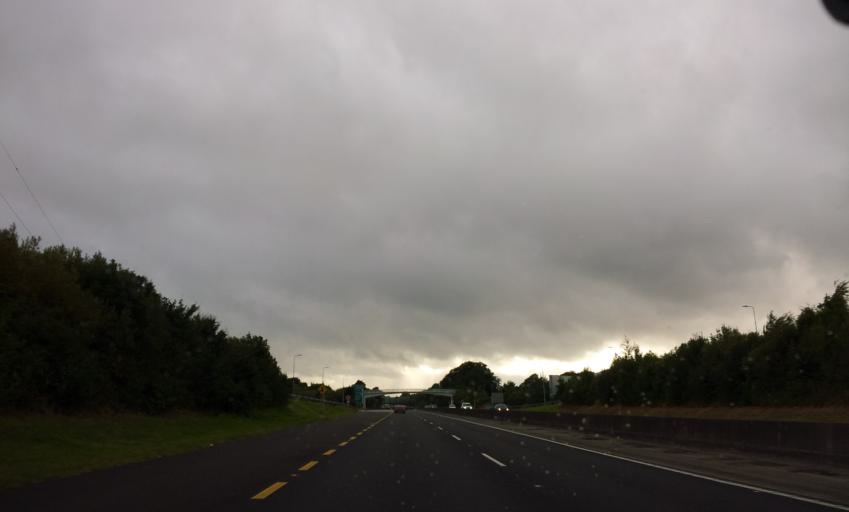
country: IE
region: Munster
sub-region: County Cork
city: Passage West
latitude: 51.8836
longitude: -8.3979
